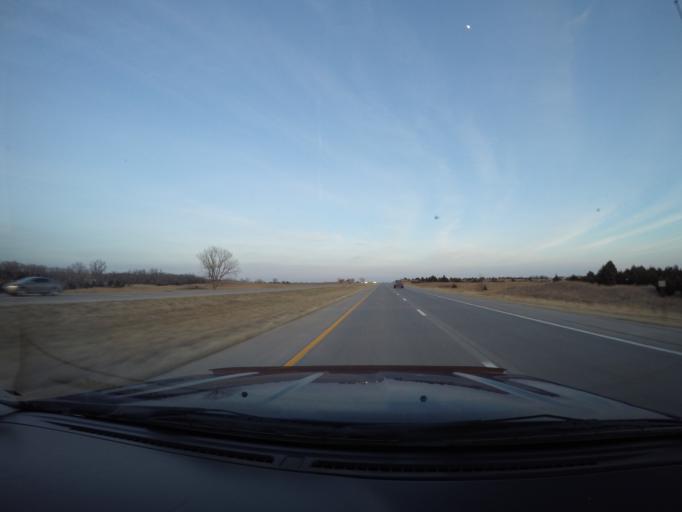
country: US
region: Kansas
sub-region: Dickinson County
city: Solomon
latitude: 38.9294
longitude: -97.3077
